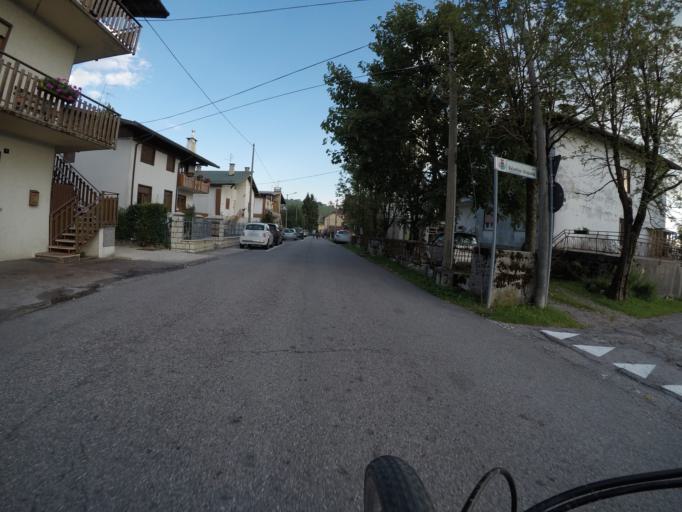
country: IT
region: Veneto
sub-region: Provincia di Vicenza
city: Gallio
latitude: 45.8908
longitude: 11.5465
